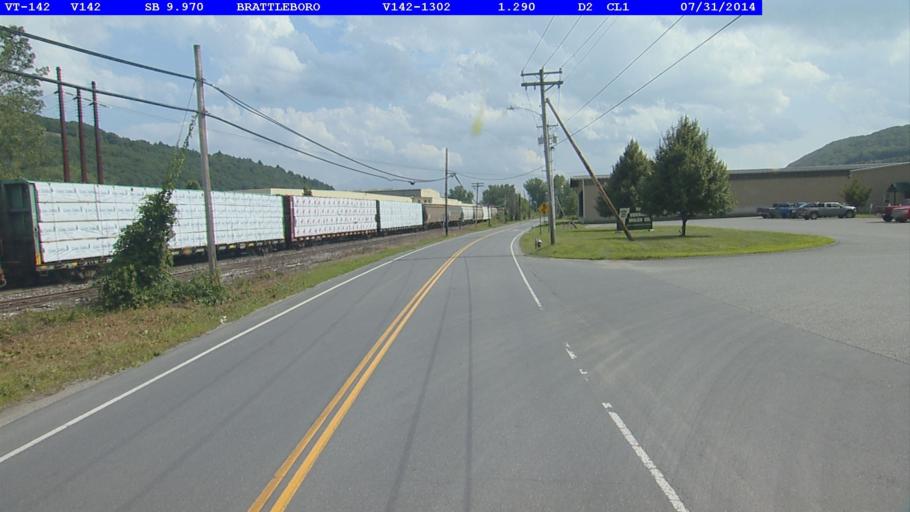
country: US
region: Vermont
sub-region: Windham County
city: Brattleboro
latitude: 42.8398
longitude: -72.5499
